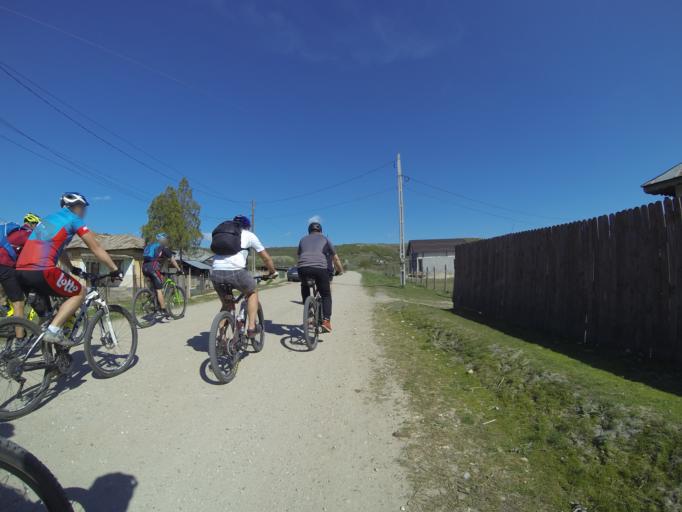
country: RO
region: Dolj
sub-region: Comuna Goesti
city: Goesti
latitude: 44.4988
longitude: 23.7551
